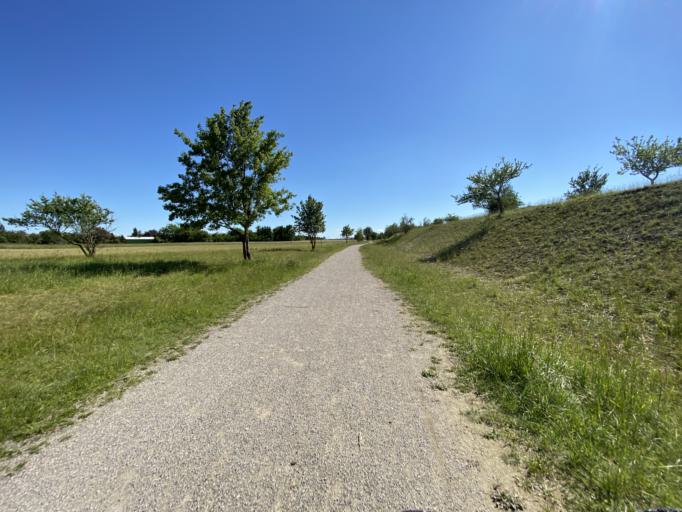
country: DE
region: Bavaria
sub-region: Upper Bavaria
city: Karlsfeld
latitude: 48.1891
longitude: 11.4433
